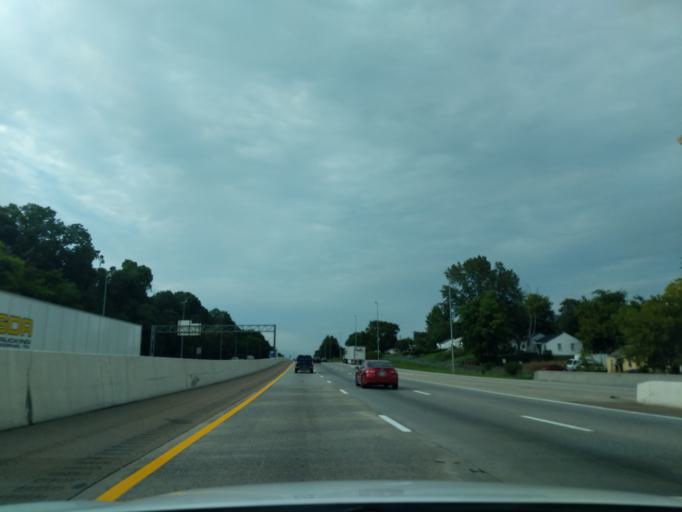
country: US
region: Tennessee
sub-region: Shelby County
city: New South Memphis
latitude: 35.0889
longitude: -90.0767
